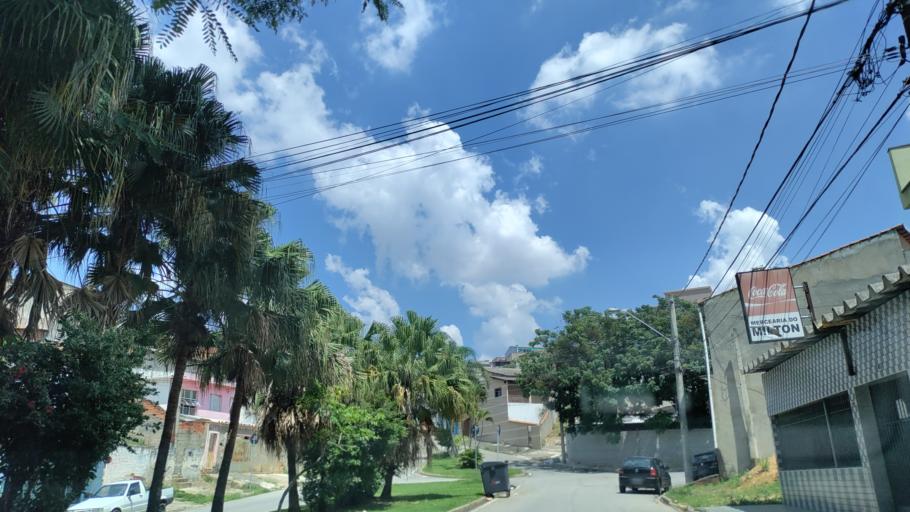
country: BR
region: Sao Paulo
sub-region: Sorocaba
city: Sorocaba
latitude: -23.4842
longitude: -47.4619
